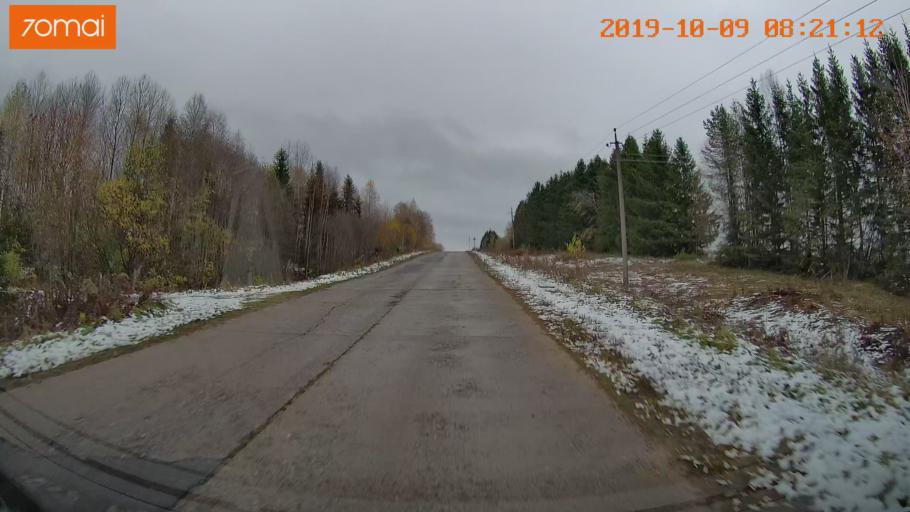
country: RU
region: Vologda
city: Gryazovets
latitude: 58.7423
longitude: 40.2729
